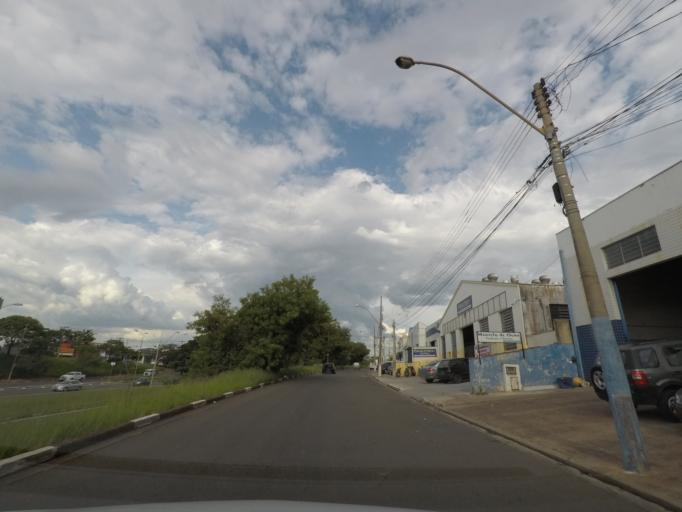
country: BR
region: Sao Paulo
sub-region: Campinas
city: Campinas
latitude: -22.8969
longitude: -47.0989
